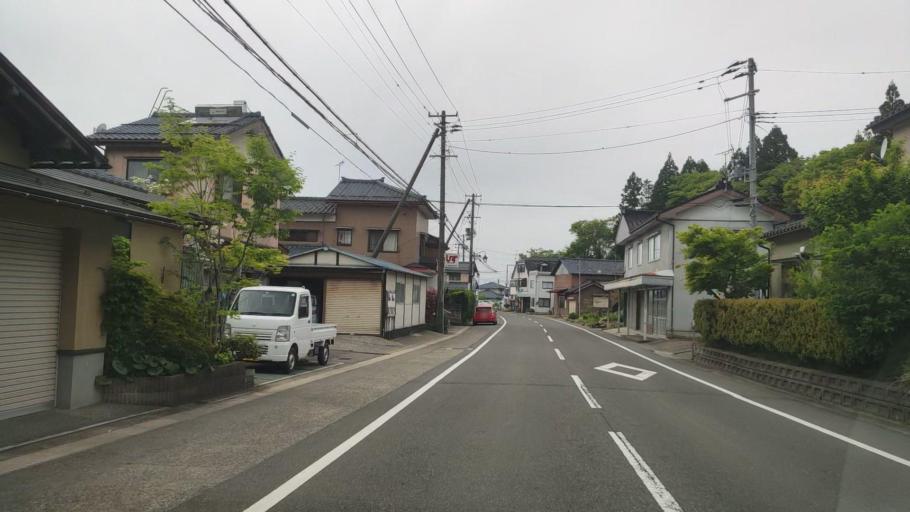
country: JP
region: Niigata
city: Kamo
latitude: 37.7124
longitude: 139.0751
